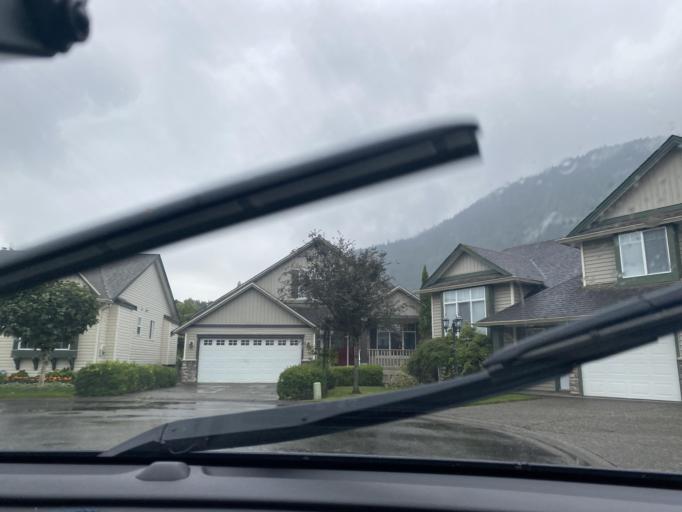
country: CA
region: British Columbia
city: Agassiz
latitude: 49.2998
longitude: -121.7822
